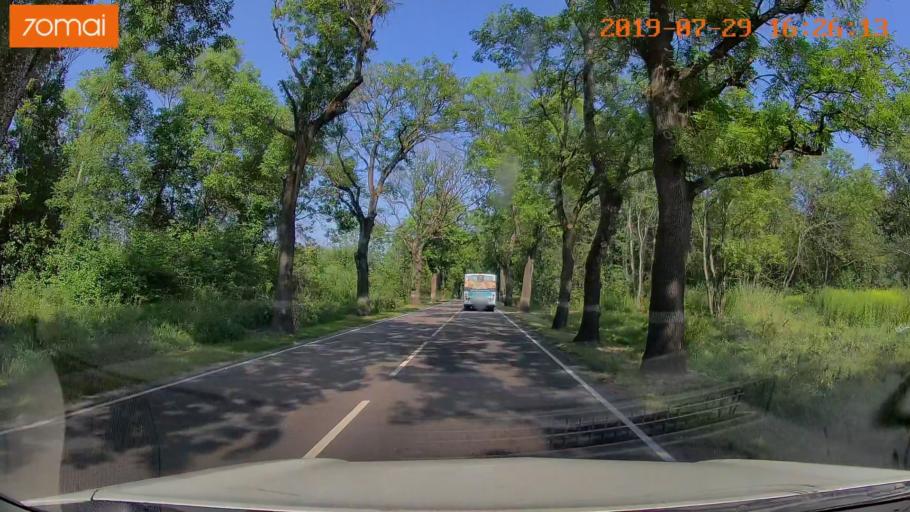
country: RU
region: Kaliningrad
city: Primorsk
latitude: 54.7276
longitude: 19.9747
